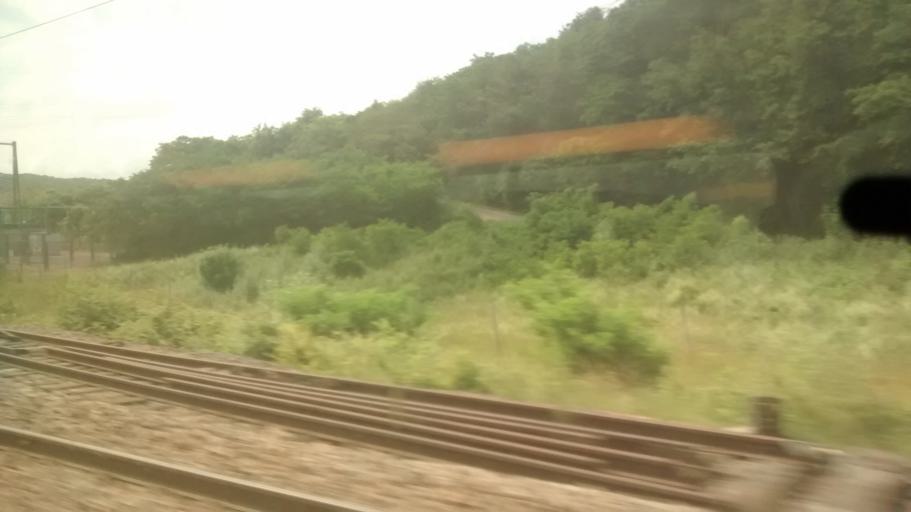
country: FR
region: Bourgogne
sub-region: Departement de Saone-et-Loire
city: Saint-Gengoux-le-National
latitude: 46.5859
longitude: 4.6127
